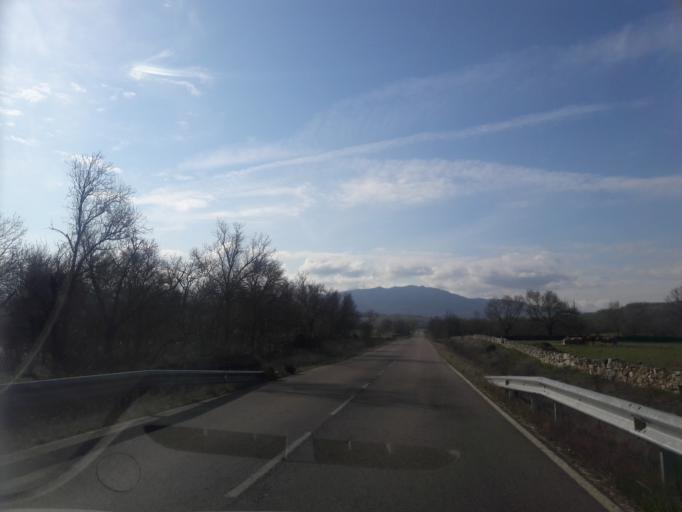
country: ES
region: Castille and Leon
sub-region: Provincia de Salamanca
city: Valdehijaderos
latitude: 40.4259
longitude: -5.8217
